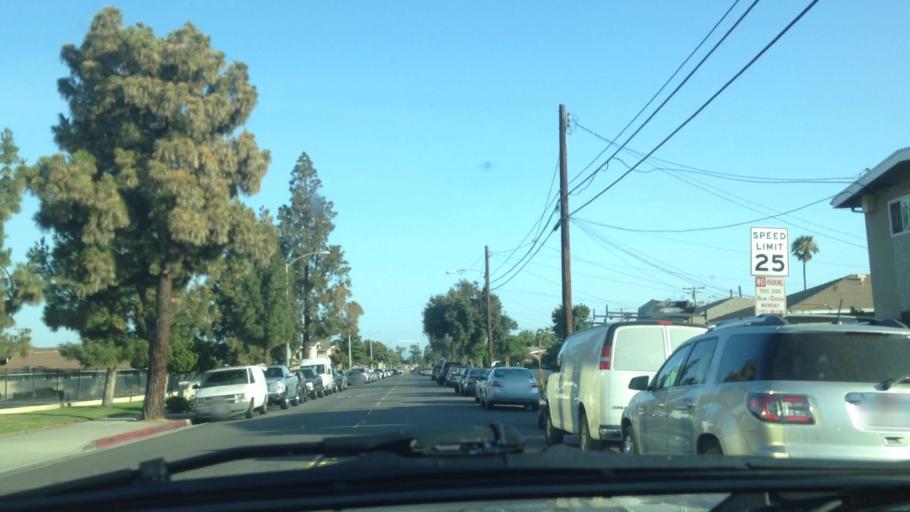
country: US
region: California
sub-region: Orange County
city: Anaheim
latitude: 33.8225
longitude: -117.9117
